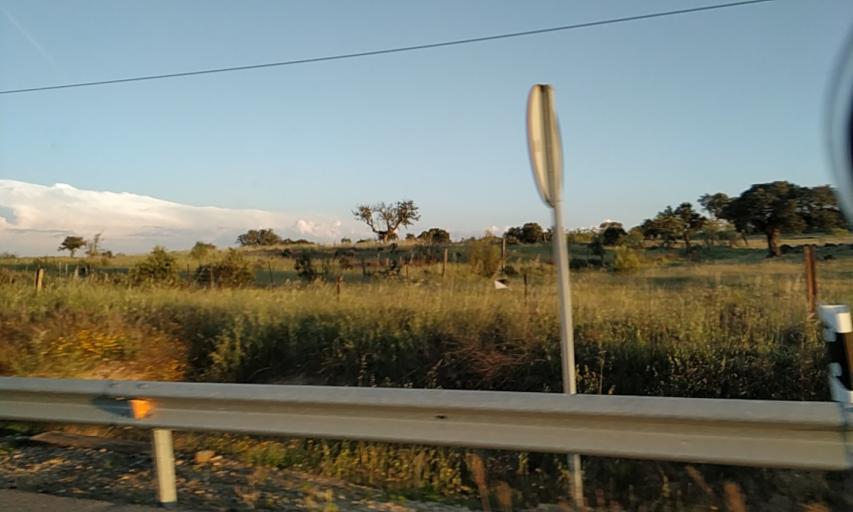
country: ES
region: Extremadura
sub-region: Provincia de Caceres
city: Salorino
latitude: 39.5136
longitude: -7.0710
